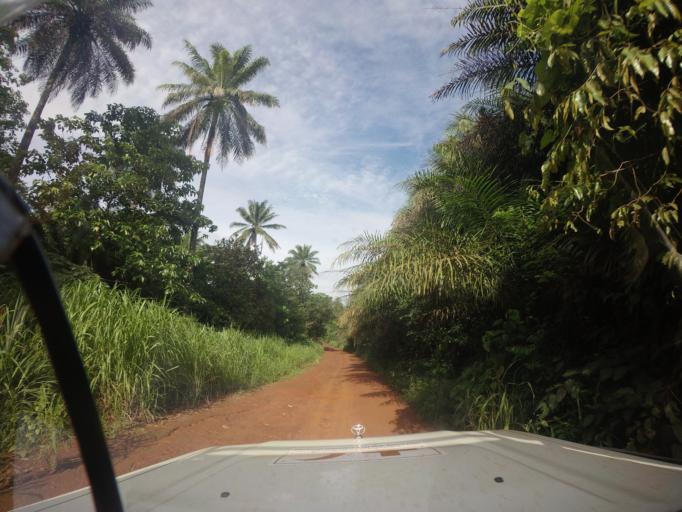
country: SL
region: Northern Province
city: Kambia
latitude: 9.1198
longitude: -12.9394
